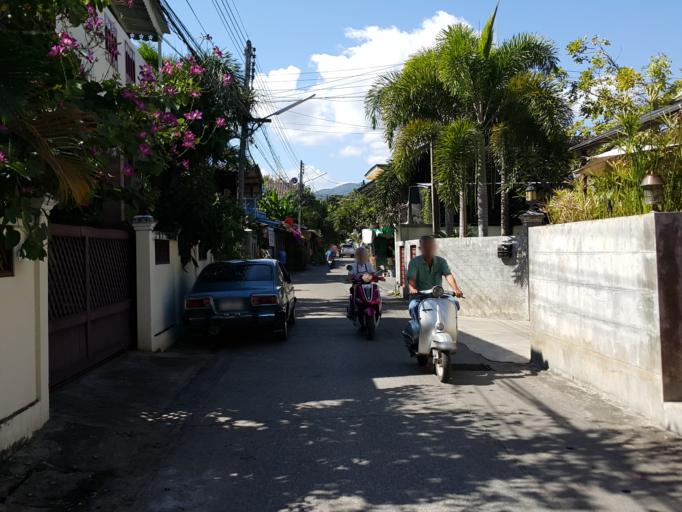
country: TH
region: Chiang Mai
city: Chiang Mai
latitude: 18.7826
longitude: 98.9846
